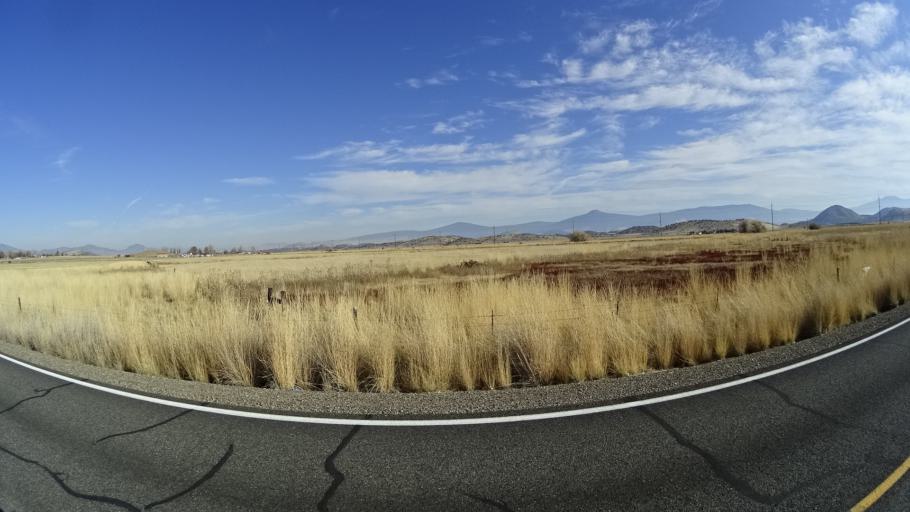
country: US
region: California
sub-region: Siskiyou County
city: Montague
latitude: 41.6057
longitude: -122.5265
